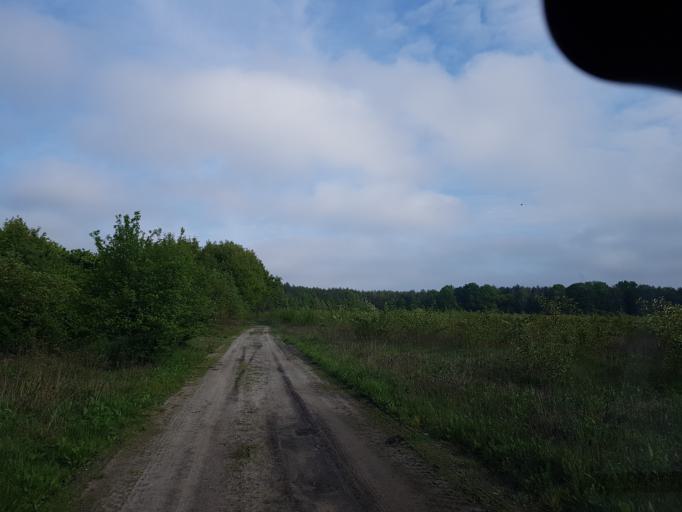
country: DE
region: Brandenburg
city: Finsterwalde
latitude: 51.5763
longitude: 13.6559
